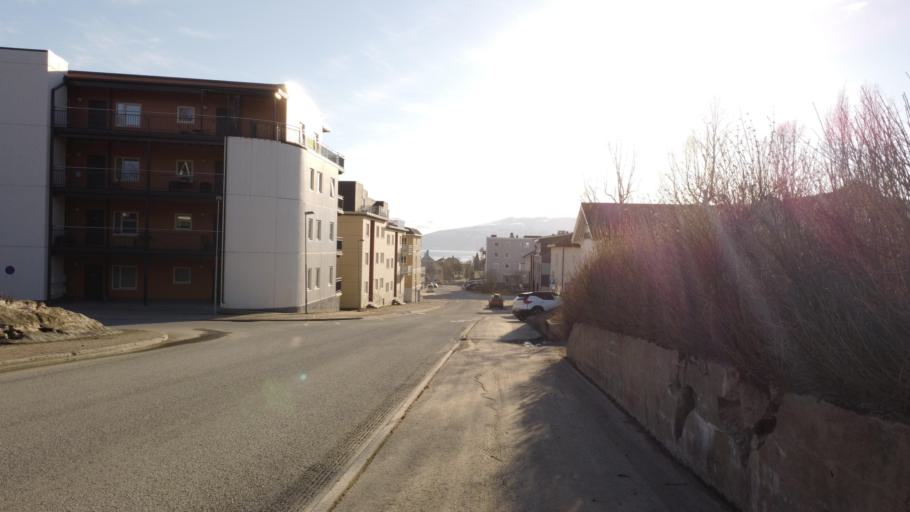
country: NO
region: Nordland
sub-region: Rana
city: Mo i Rana
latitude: 66.3131
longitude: 14.1386
